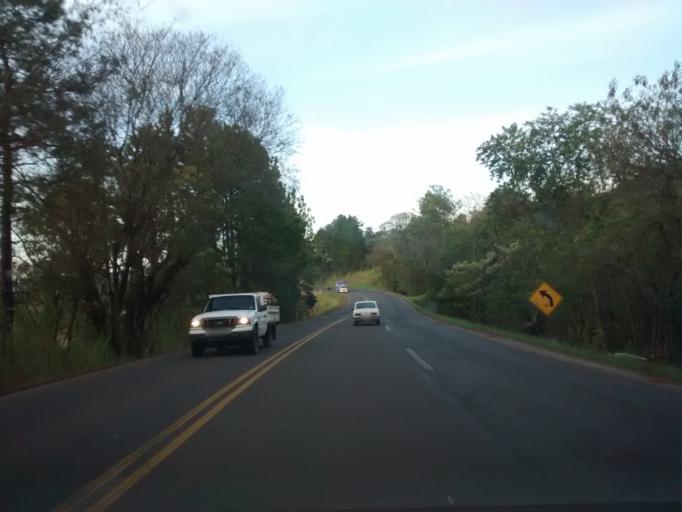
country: BR
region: Parana
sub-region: Francisco Beltrao
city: Francisco Beltrao
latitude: -26.0936
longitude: -53.0602
